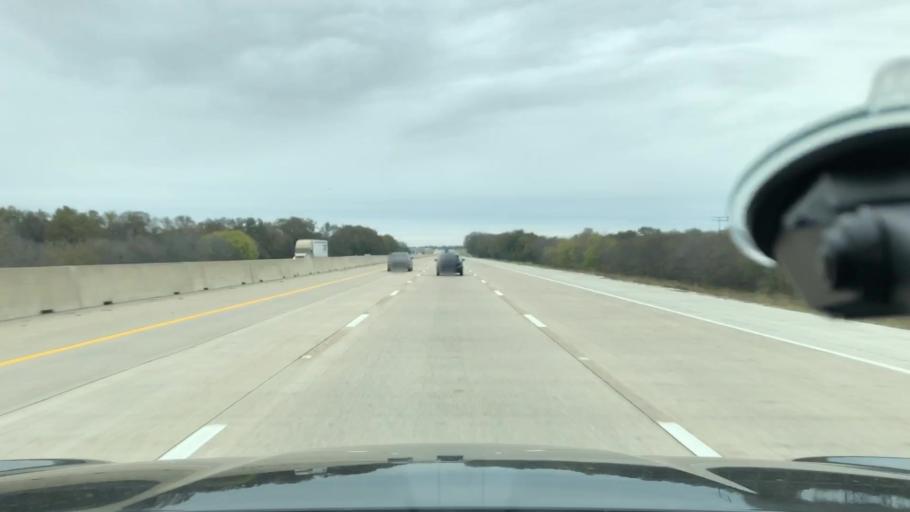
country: US
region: Texas
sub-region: Ellis County
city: Italy
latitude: 32.2255
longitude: -96.8851
